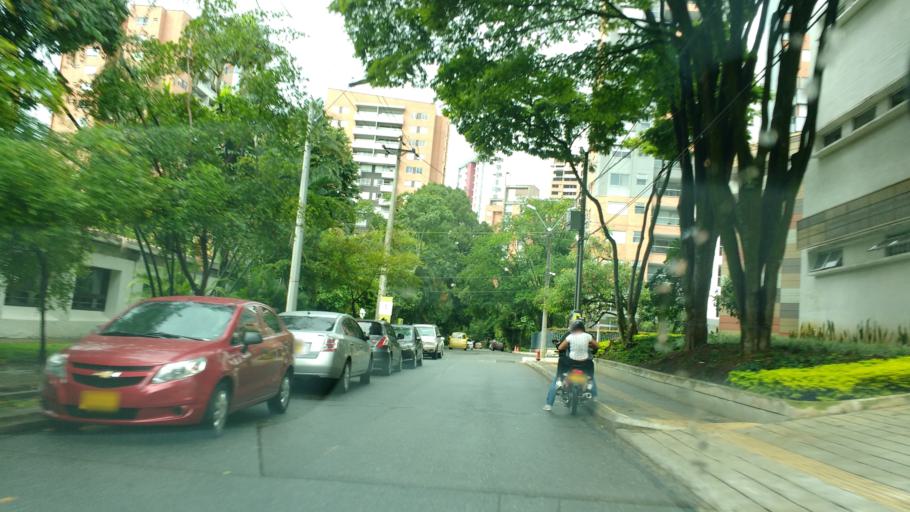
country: CO
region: Antioquia
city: Envigado
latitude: 6.1903
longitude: -75.5785
